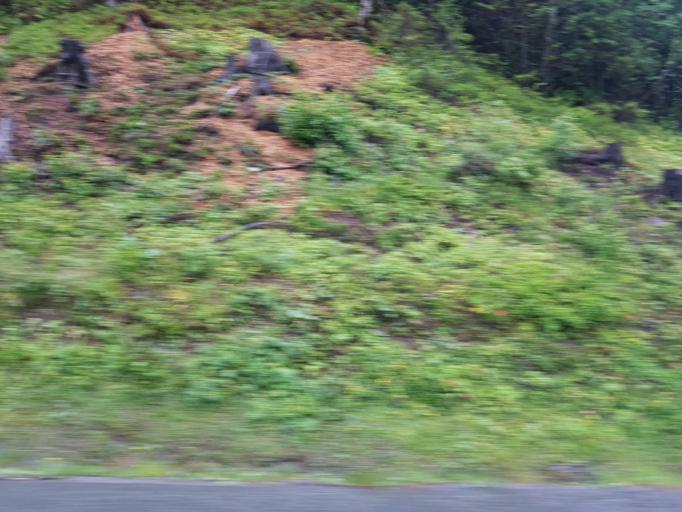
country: NO
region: Sor-Trondelag
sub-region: Selbu
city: Mebonden
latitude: 63.3326
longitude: 11.0915
